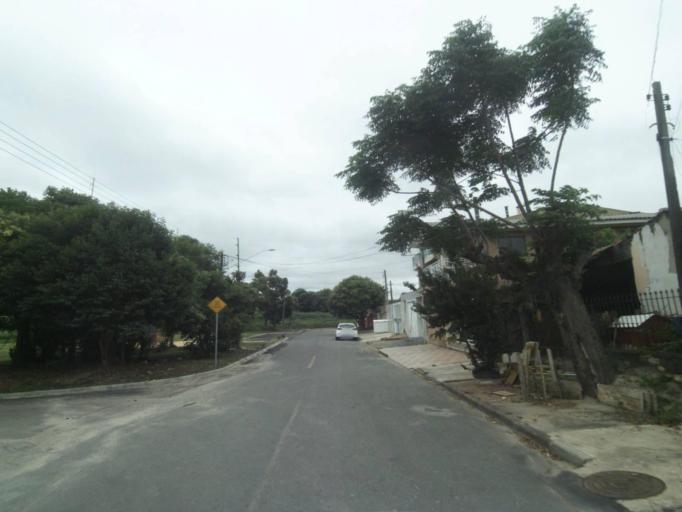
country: BR
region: Parana
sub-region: Araucaria
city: Araucaria
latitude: -25.5279
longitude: -49.3390
